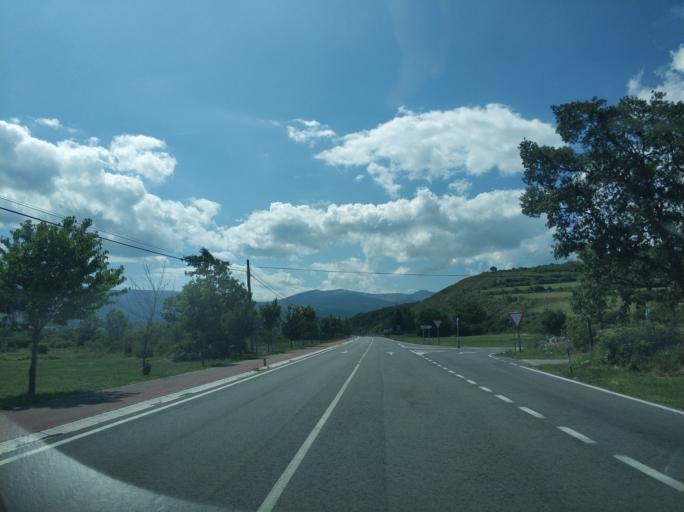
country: ES
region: Cantabria
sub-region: Provincia de Cantabria
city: Villaescusa
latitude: 43.0207
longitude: -4.2388
